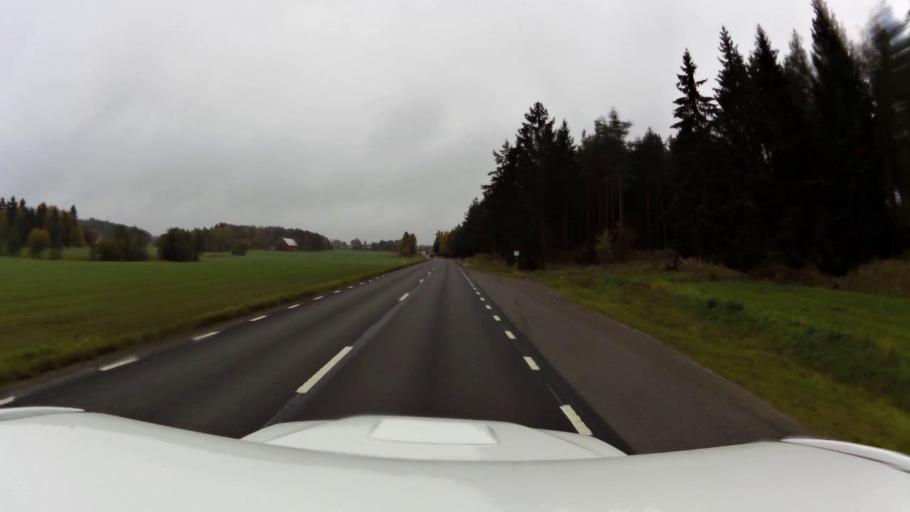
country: SE
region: OEstergoetland
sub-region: Linkopings Kommun
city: Linghem
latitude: 58.3633
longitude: 15.8244
